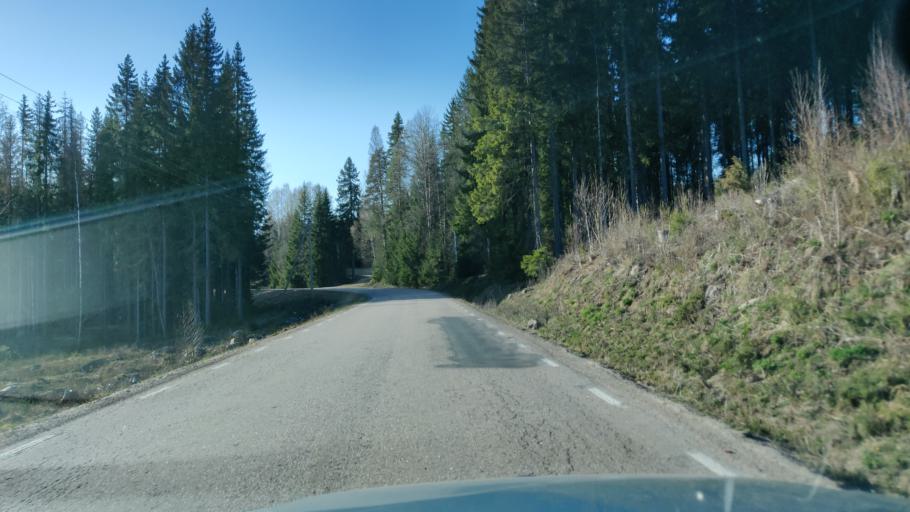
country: SE
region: Vaermland
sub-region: Munkfors Kommun
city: Munkfors
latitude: 59.9850
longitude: 13.3984
